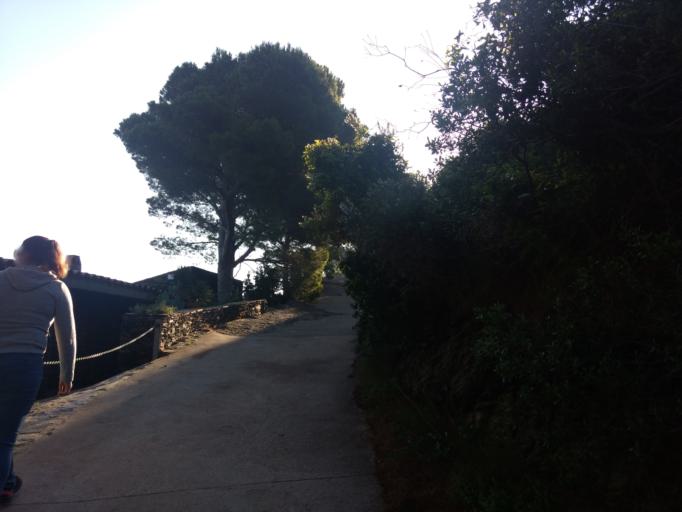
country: ES
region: Catalonia
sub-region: Provincia de Girona
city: Cadaques
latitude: 42.2782
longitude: 3.2771
